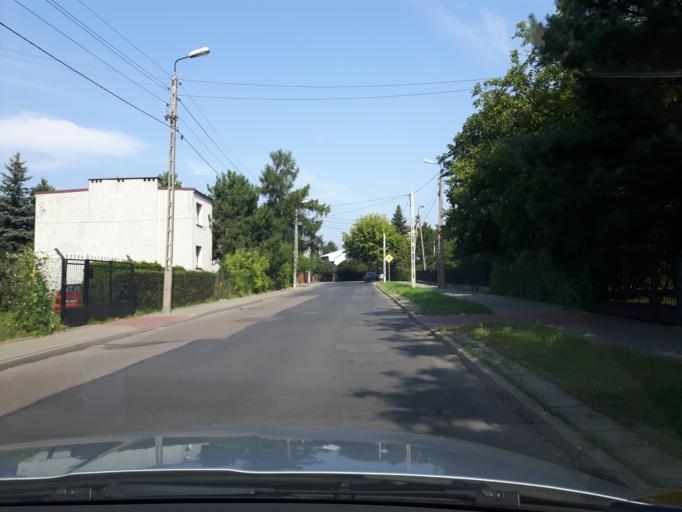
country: PL
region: Masovian Voivodeship
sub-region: Warszawa
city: Targowek
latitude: 52.2770
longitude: 21.0733
